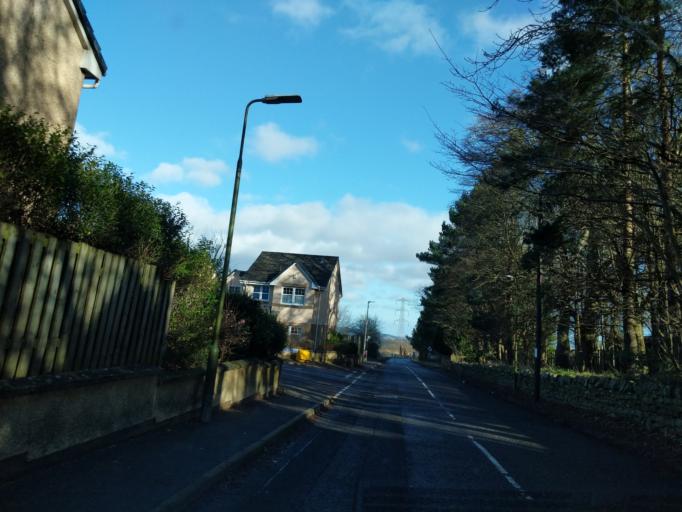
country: GB
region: Scotland
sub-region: West Lothian
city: Kirknewton
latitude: 55.8901
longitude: -3.4125
